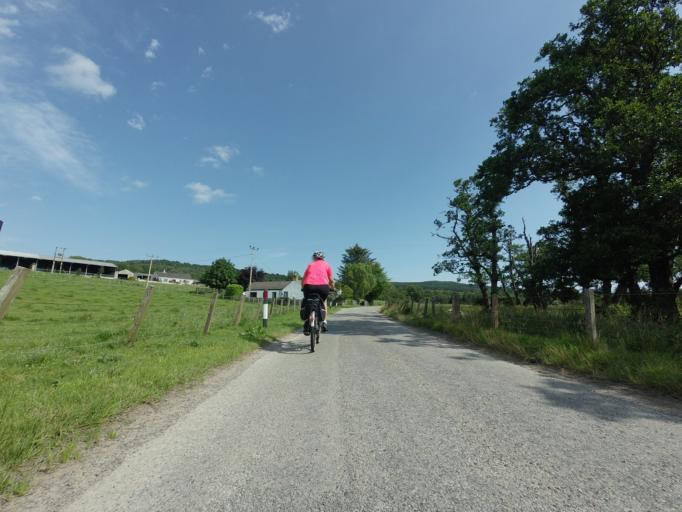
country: GB
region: Scotland
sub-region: Highland
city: Invergordon
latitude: 57.7520
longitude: -4.1601
